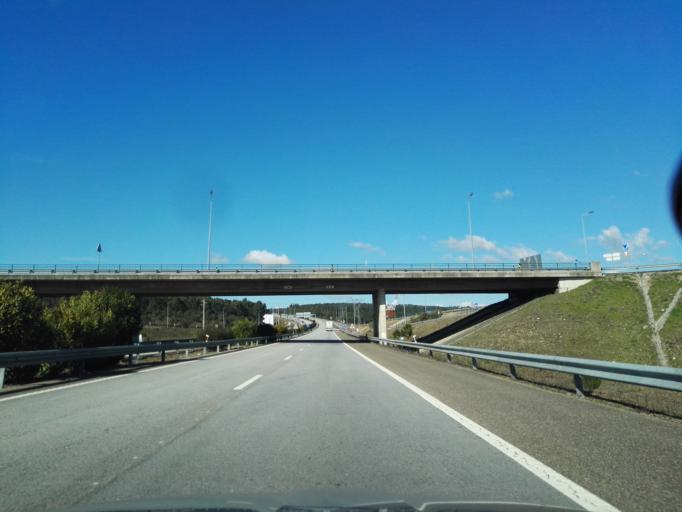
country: PT
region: Santarem
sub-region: Abrantes
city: Alferrarede
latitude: 39.4911
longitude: -8.1763
